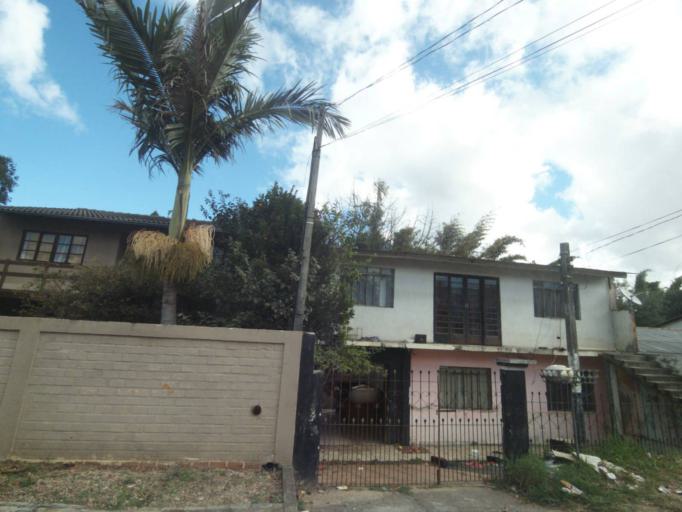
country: BR
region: Parana
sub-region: Sao Jose Dos Pinhais
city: Sao Jose dos Pinhais
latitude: -25.5339
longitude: -49.2848
